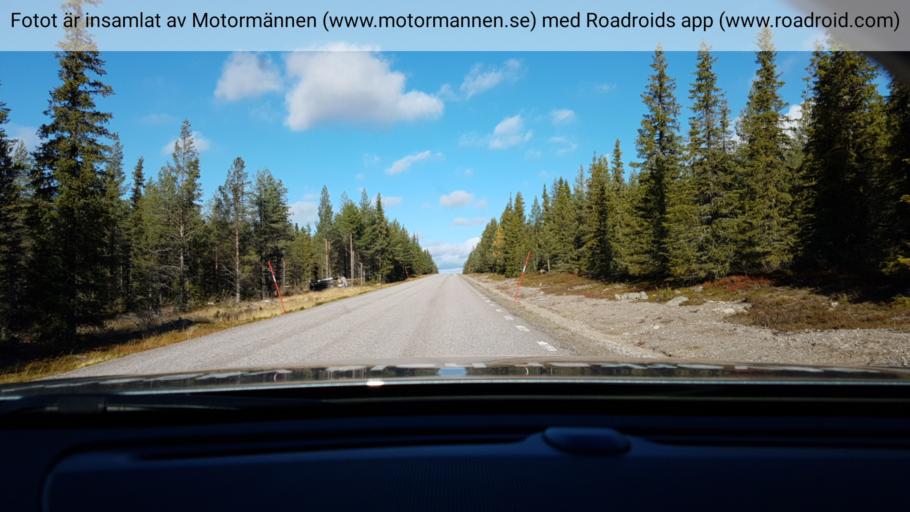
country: SE
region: Norrbotten
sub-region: Arjeplogs Kommun
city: Arjeplog
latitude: 65.8294
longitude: 18.4338
